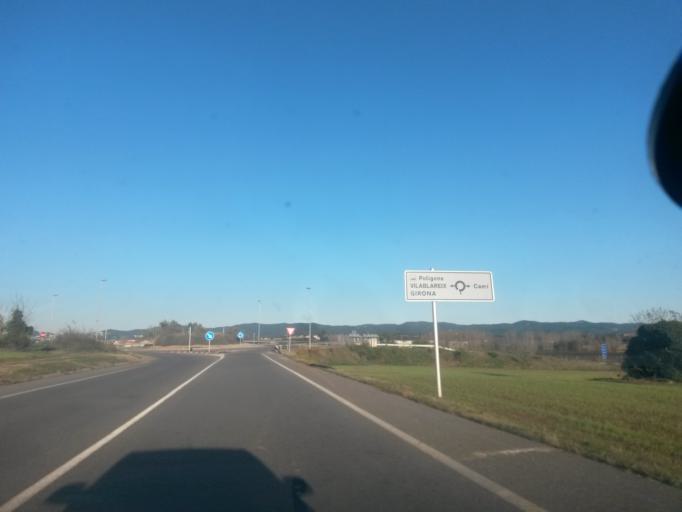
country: ES
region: Catalonia
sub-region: Provincia de Girona
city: Vilablareix
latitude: 41.9424
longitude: 2.7870
